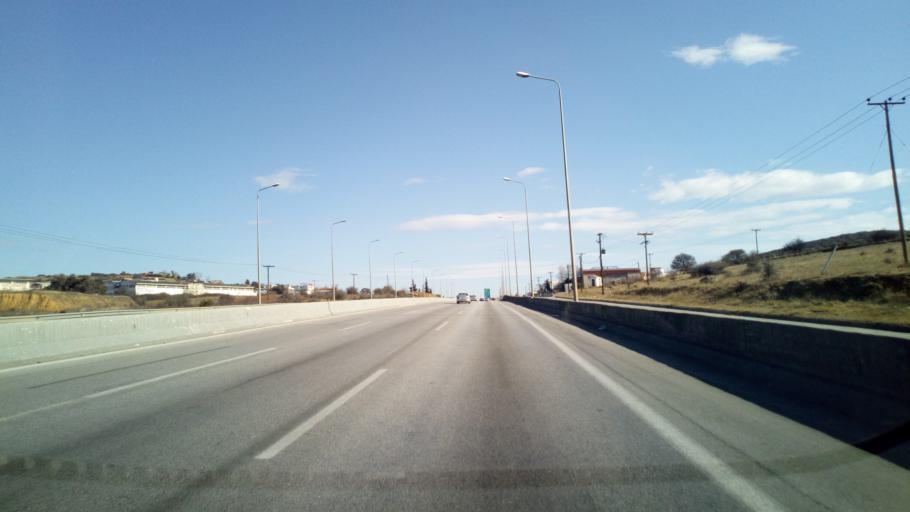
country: GR
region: Central Macedonia
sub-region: Nomos Thessalonikis
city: Liti
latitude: 40.7181
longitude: 22.9679
